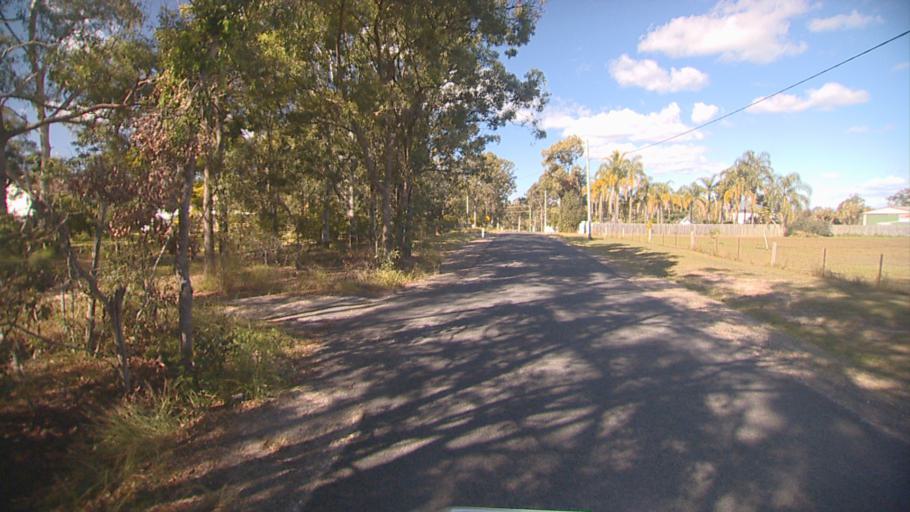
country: AU
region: Queensland
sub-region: Logan
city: Logan Reserve
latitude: -27.7258
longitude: 153.0961
